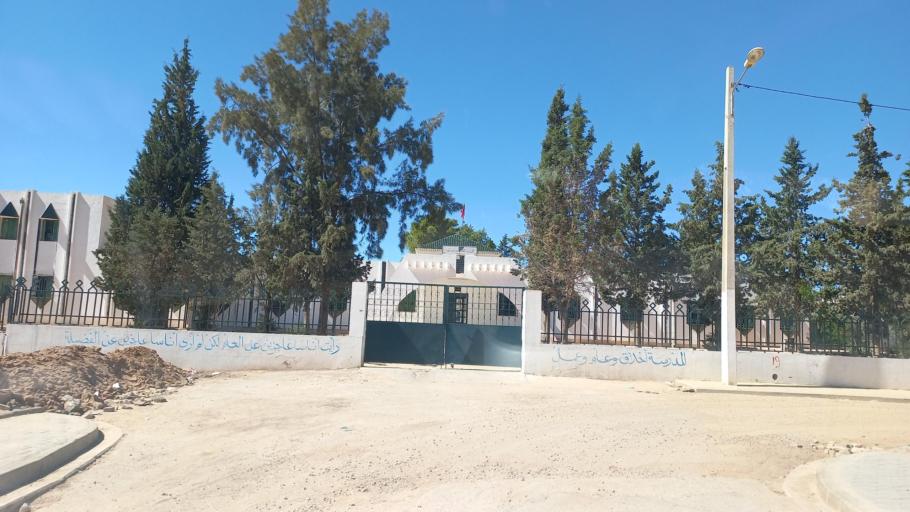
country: TN
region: Al Qasrayn
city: Sbiba
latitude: 35.3586
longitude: 9.0916
